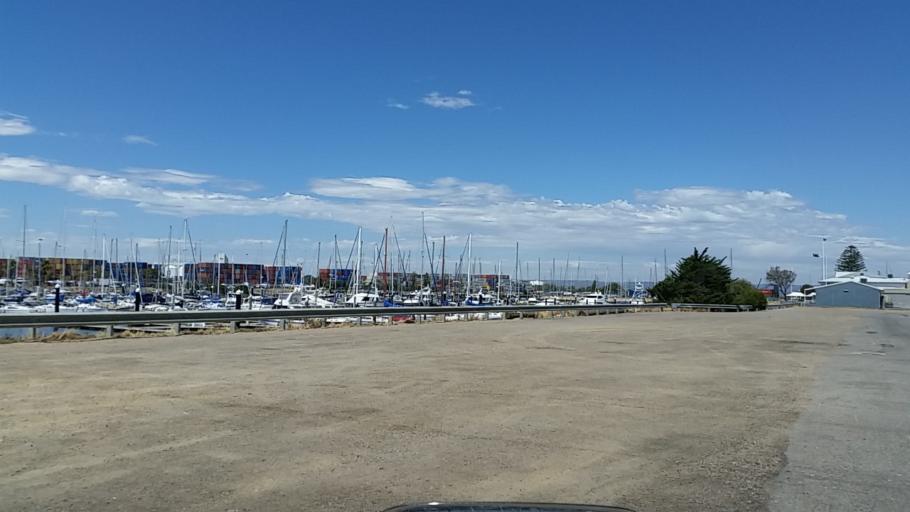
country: AU
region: South Australia
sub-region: Port Adelaide Enfield
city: Birkenhead
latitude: -34.7746
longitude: 138.4864
